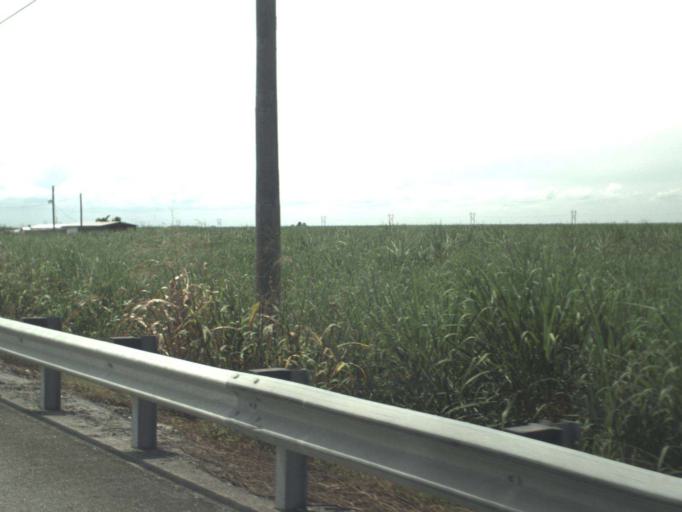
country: US
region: Florida
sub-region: Palm Beach County
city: Pahokee
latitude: 26.8005
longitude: -80.6534
